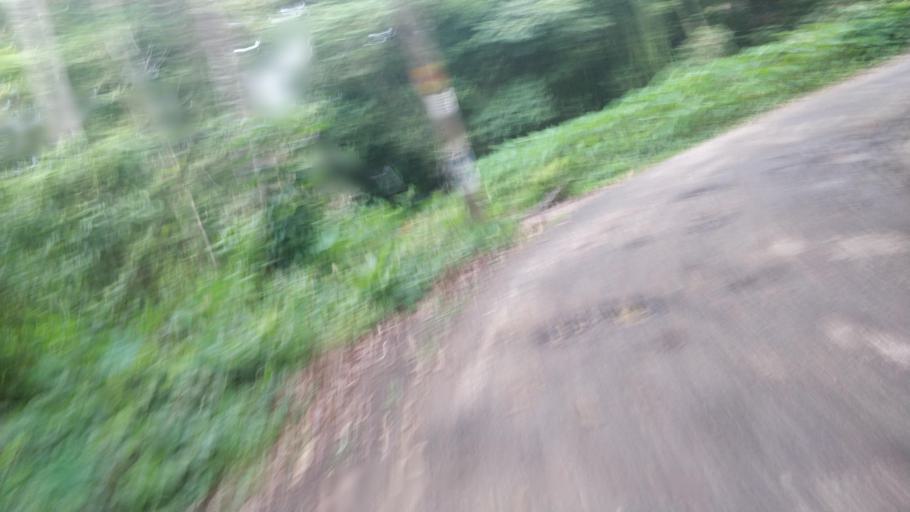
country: IN
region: Kerala
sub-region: Alappuzha
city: Vayalar
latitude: 9.7045
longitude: 76.3527
